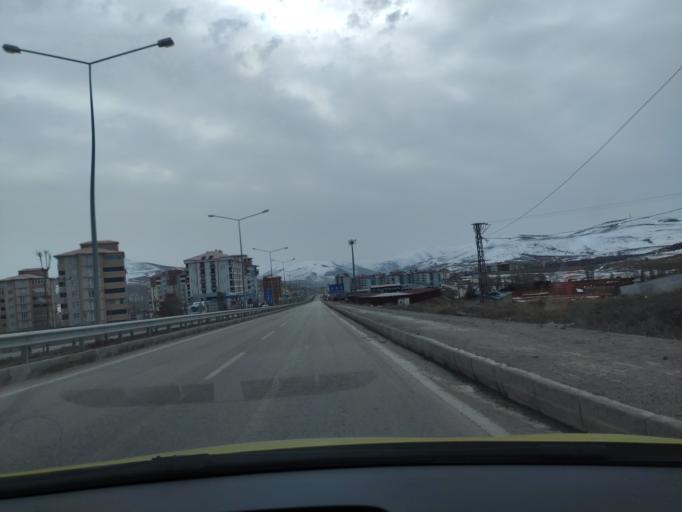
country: TR
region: Bayburt
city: Bayburt
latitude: 40.2714
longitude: 40.1941
